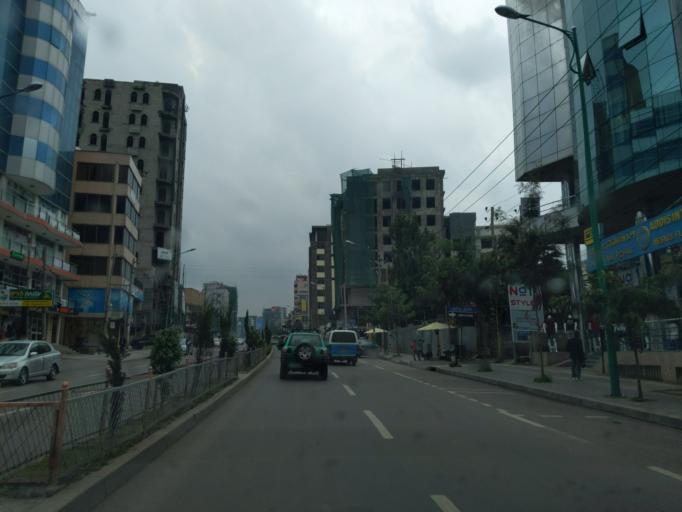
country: ET
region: Adis Abeba
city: Addis Ababa
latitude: 8.9933
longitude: 38.7665
